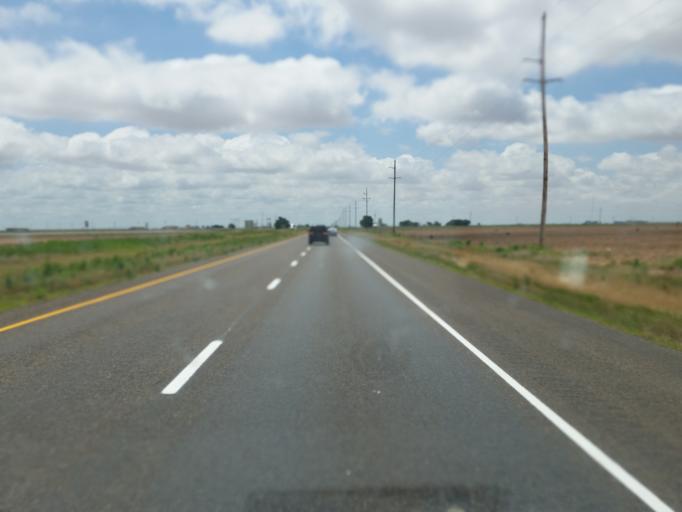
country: US
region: Texas
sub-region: Lubbock County
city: Slaton
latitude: 33.4079
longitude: -101.6238
